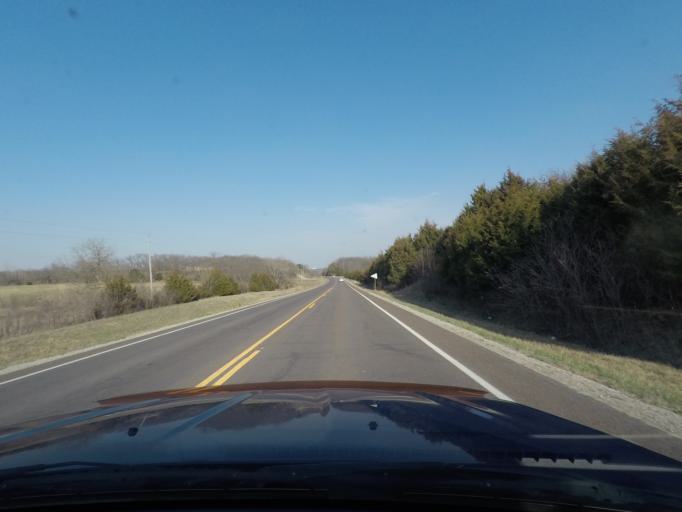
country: US
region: Kansas
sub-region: Douglas County
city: Lawrence
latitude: 39.0006
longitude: -95.3126
